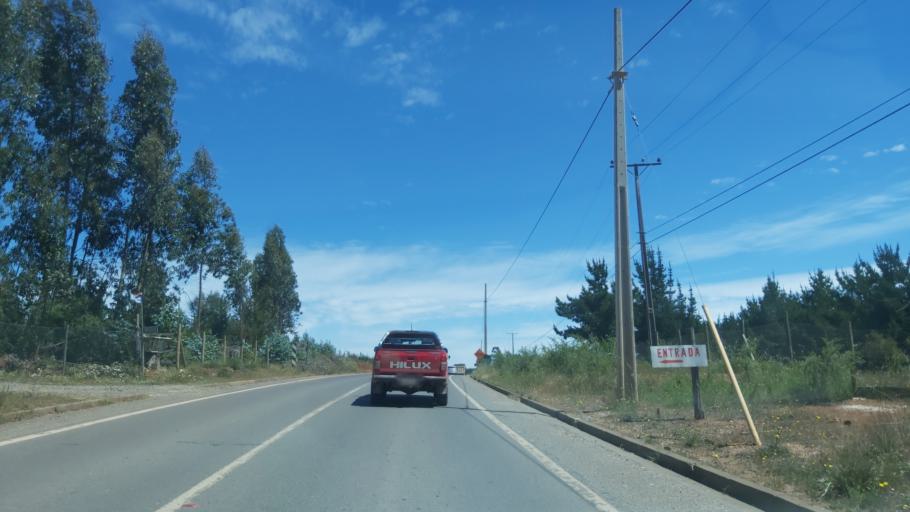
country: CL
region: Maule
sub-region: Provincia de Talca
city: Constitucion
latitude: -35.3997
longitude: -72.4362
